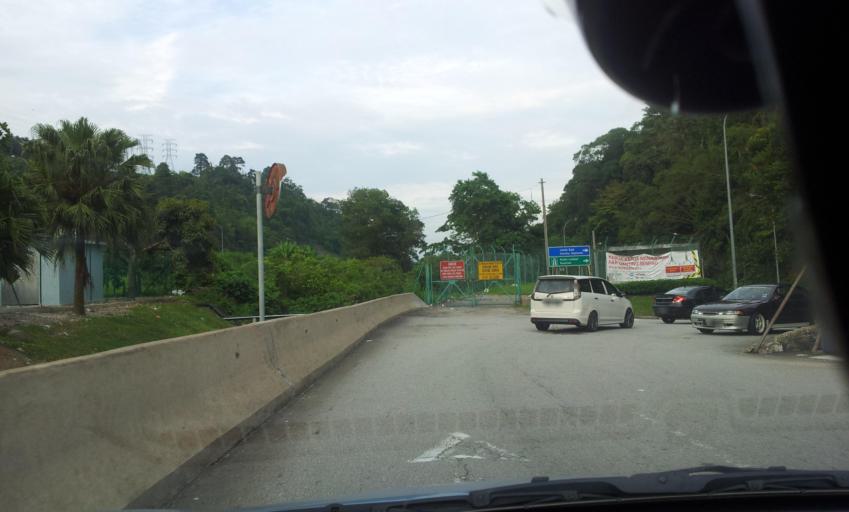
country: MY
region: Pahang
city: Kampung Bukit Tinggi, Bentong
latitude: 3.3522
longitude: 101.7922
